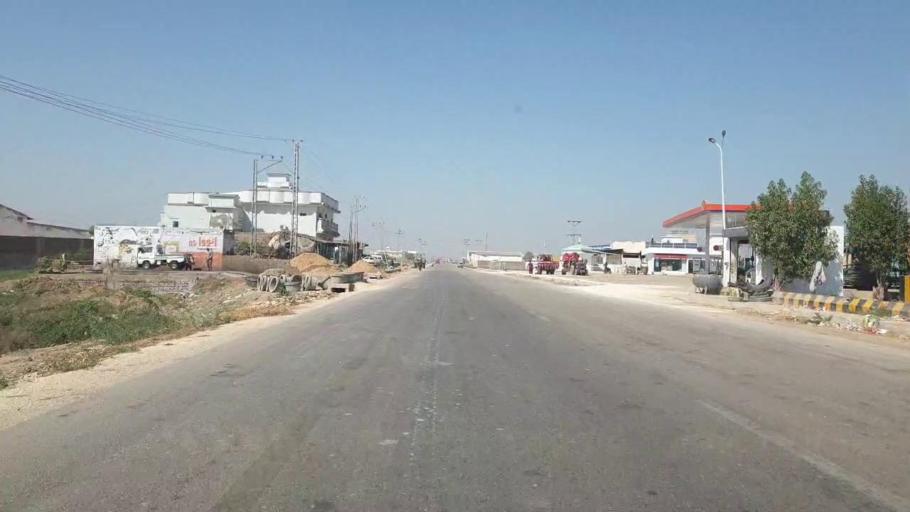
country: PK
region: Sindh
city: Talhar
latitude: 24.8742
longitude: 68.8160
